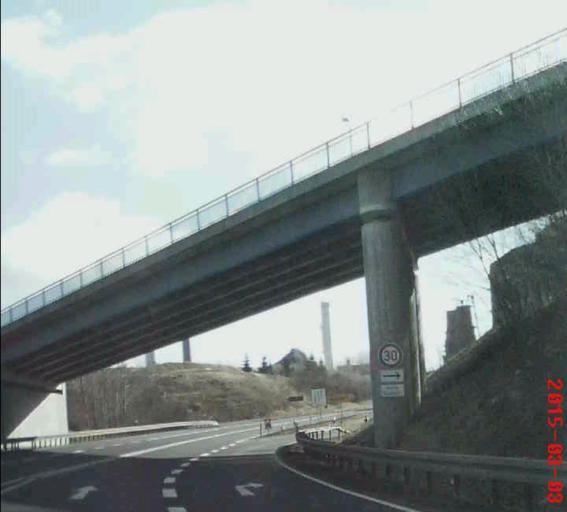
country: DE
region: Thuringia
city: Unterwellenborn
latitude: 50.6565
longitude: 11.4217
